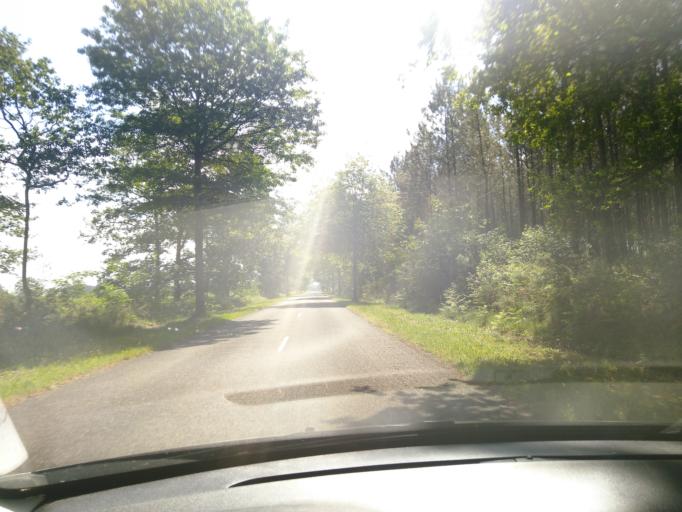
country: FR
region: Aquitaine
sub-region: Departement des Landes
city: Saint-Vincent-de-Paul
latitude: 43.7841
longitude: -0.9824
